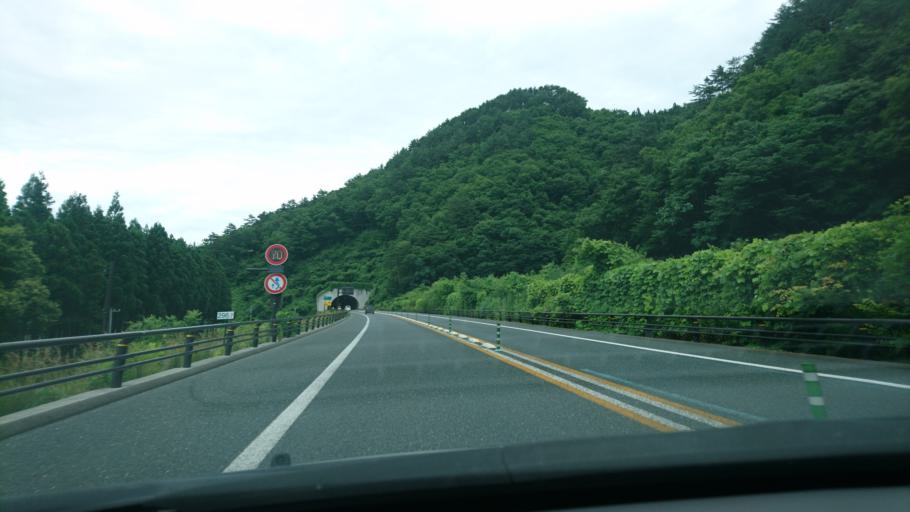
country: JP
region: Iwate
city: Miyako
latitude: 39.8464
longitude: 141.9513
